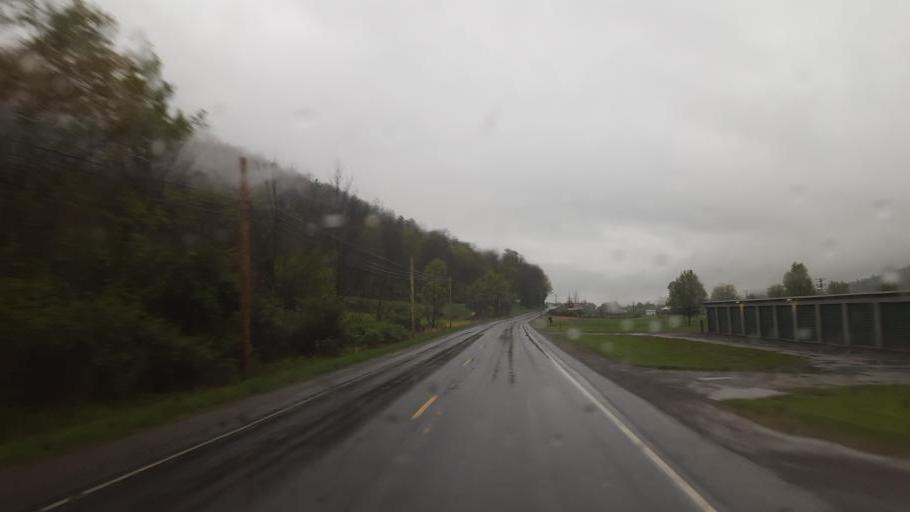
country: US
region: Pennsylvania
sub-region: Tioga County
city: Westfield
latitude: 41.9547
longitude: -77.4548
